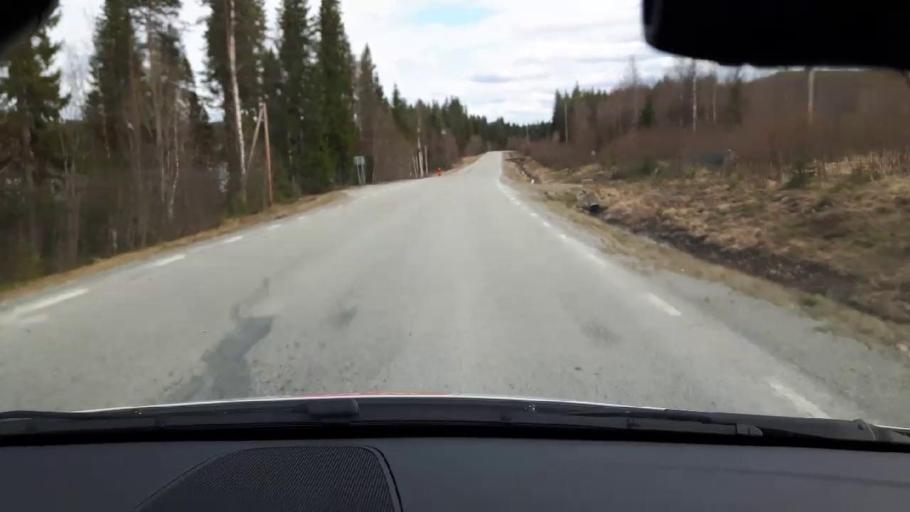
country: SE
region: Jaemtland
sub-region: Bergs Kommun
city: Hoverberg
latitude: 62.6644
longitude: 14.7320
